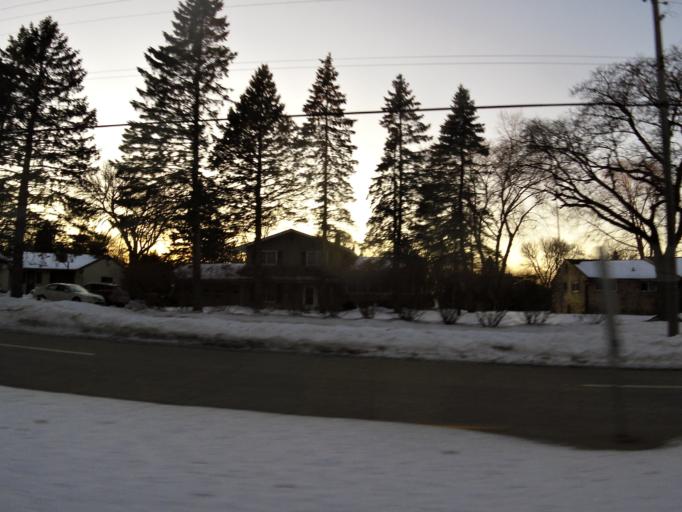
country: US
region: Minnesota
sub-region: Ramsey County
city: White Bear Lake
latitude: 45.0579
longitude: -93.0154
